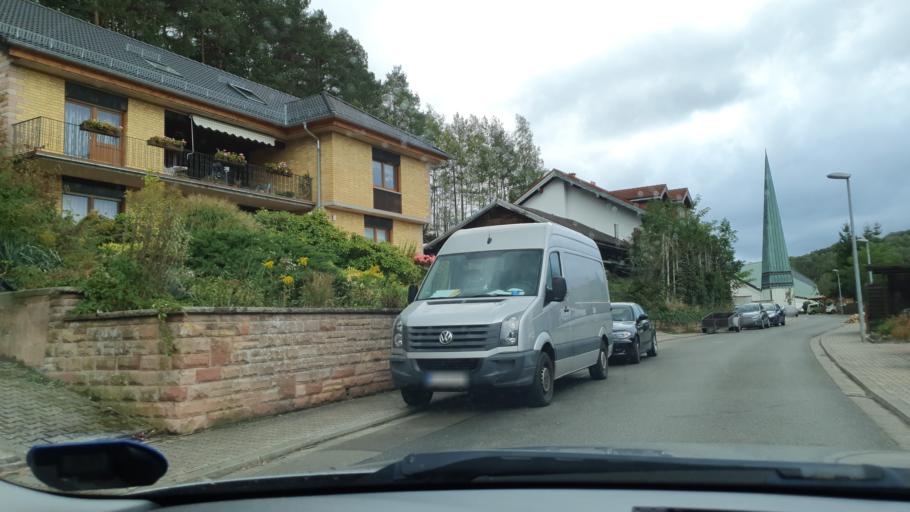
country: DE
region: Rheinland-Pfalz
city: Krickenbach
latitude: 49.3635
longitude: 7.6711
